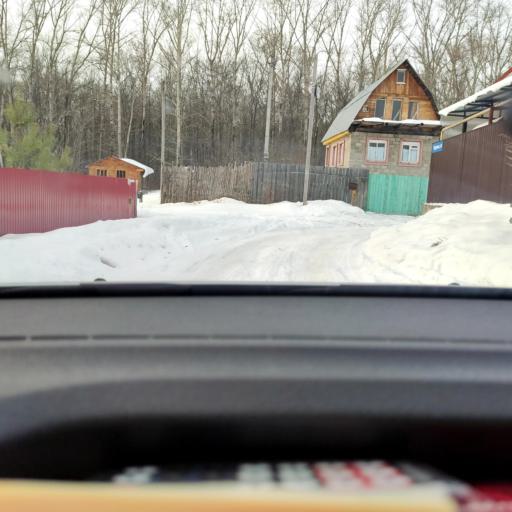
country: RU
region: Bashkortostan
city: Ufa
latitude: 54.7103
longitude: 55.9258
